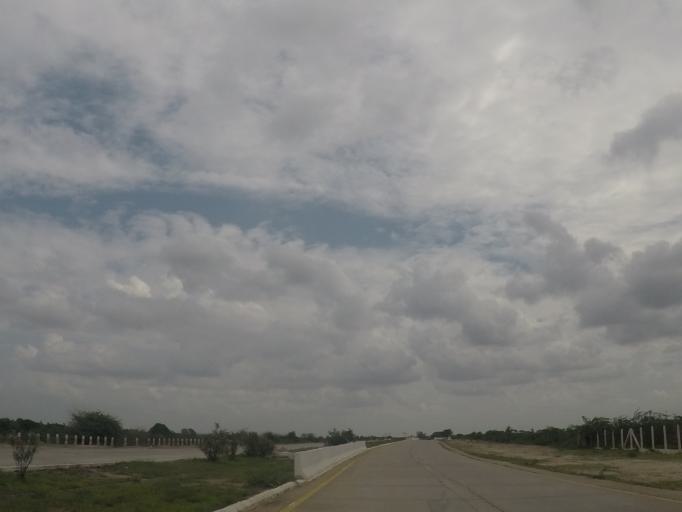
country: MM
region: Mandalay
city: Kyaukse
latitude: 21.6728
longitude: 95.9915
